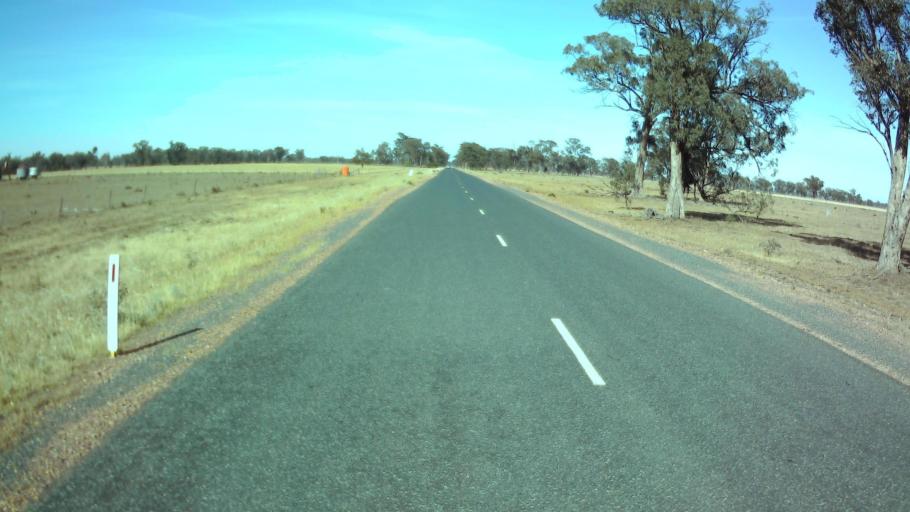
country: AU
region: New South Wales
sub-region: Weddin
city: Grenfell
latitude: -34.0987
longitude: 147.8810
